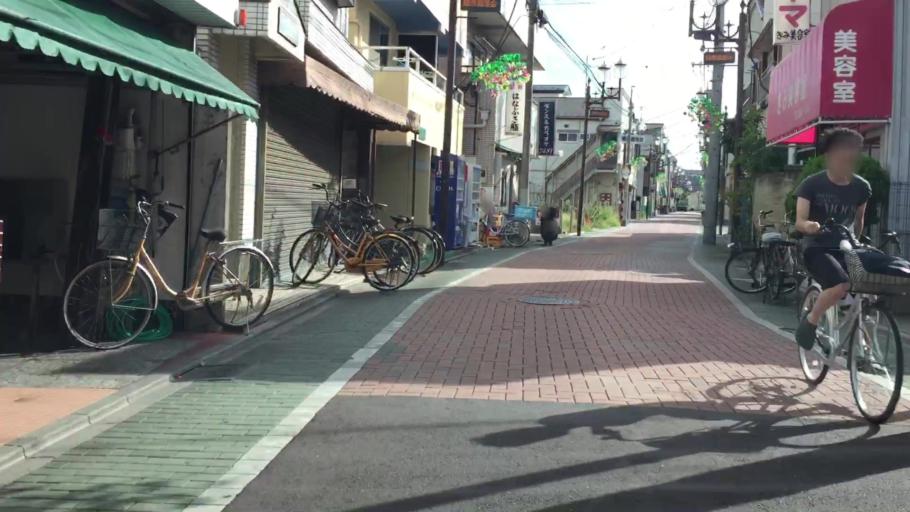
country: JP
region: Saitama
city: Soka
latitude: 35.7711
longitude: 139.7899
